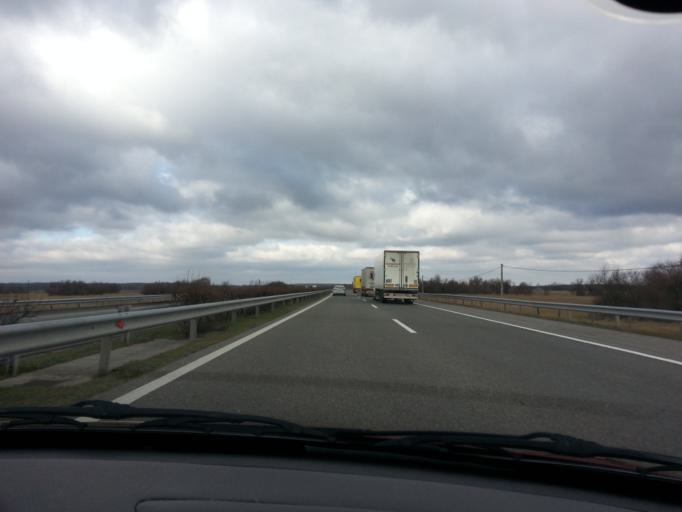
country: HU
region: Csongrad
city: Csengele
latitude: 46.5626
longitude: 19.8805
